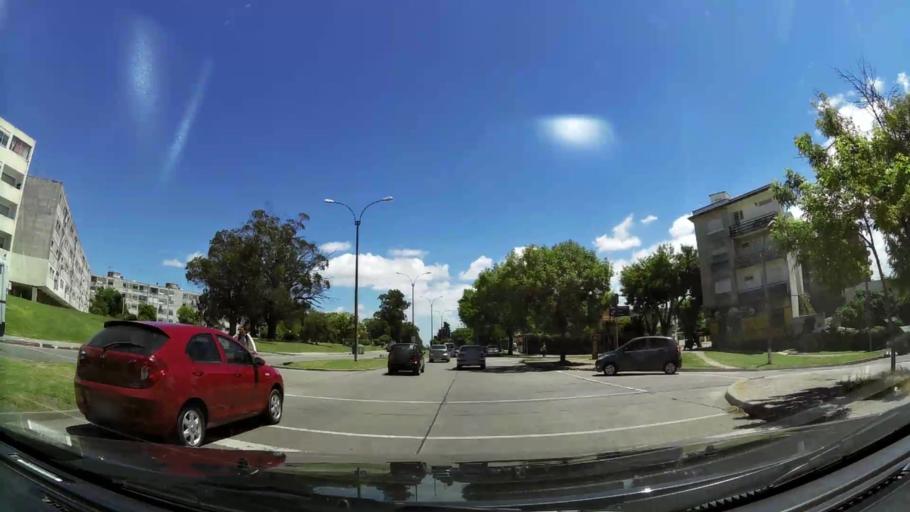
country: UY
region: Montevideo
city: Montevideo
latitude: -34.8962
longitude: -56.1260
